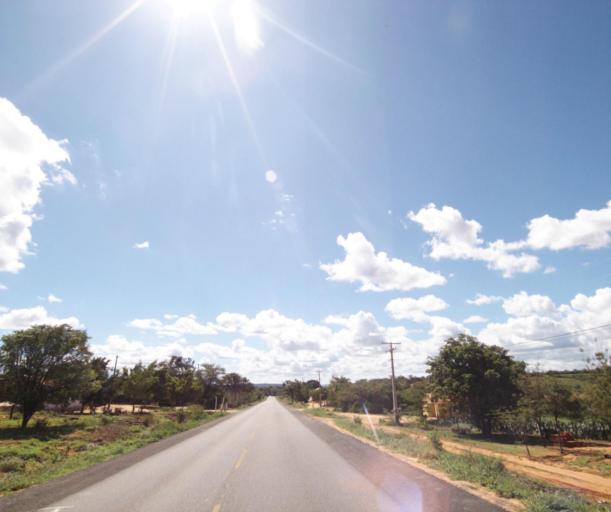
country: BR
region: Bahia
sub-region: Cacule
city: Cacule
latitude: -14.1920
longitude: -42.1507
